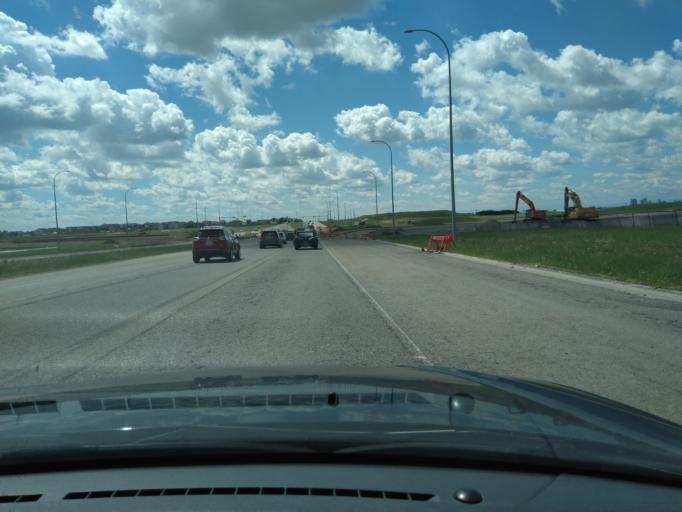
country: CA
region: Alberta
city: Calgary
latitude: 51.1421
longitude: -113.9702
